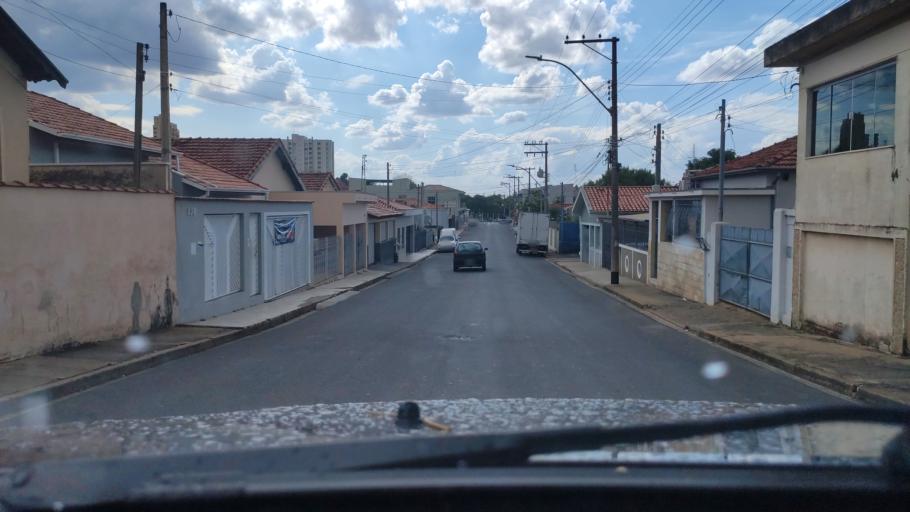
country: BR
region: Sao Paulo
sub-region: Itapira
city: Itapira
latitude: -22.4387
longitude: -46.8153
